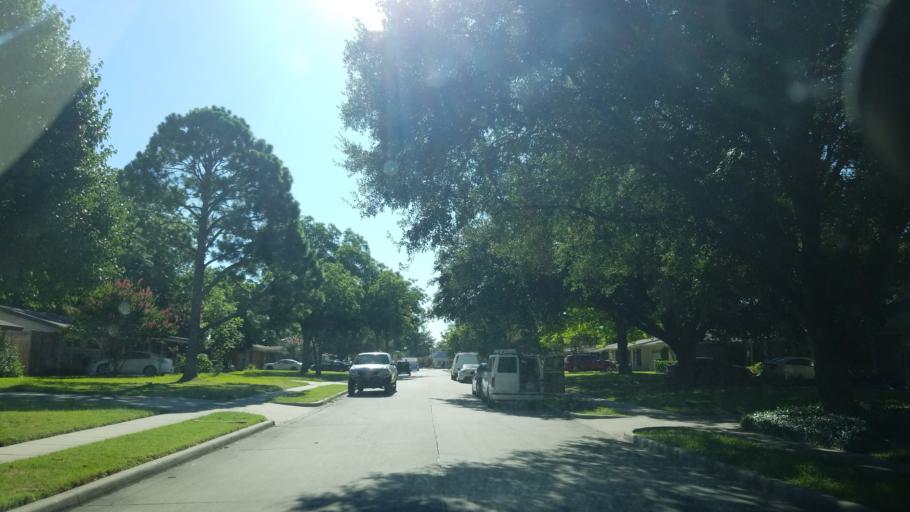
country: US
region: Texas
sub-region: Dallas County
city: Carrollton
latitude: 32.9518
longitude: -96.8925
